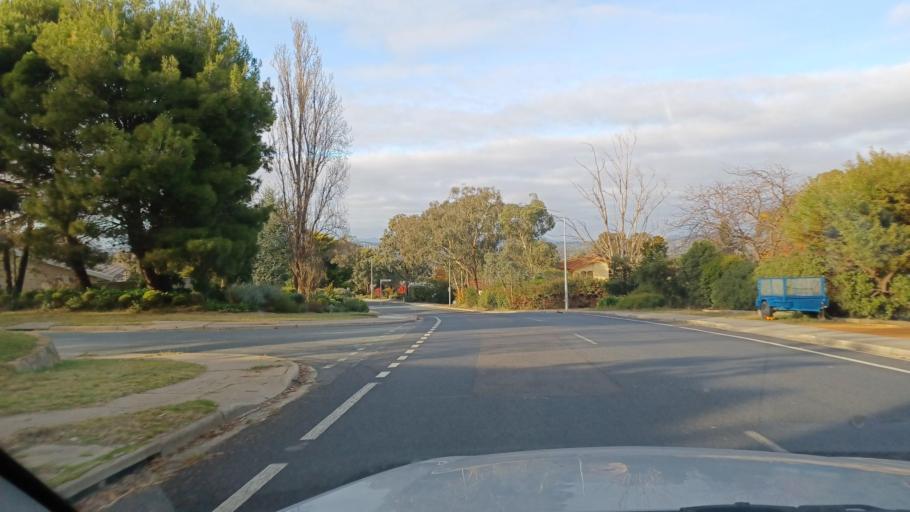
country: AU
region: Australian Capital Territory
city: Belconnen
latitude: -35.2023
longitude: 149.0498
